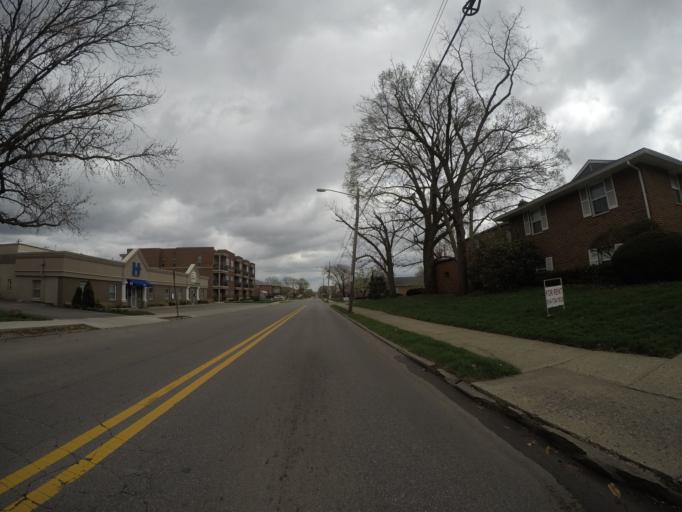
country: US
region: Ohio
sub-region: Franklin County
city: Grandview Heights
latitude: 39.9916
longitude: -83.0449
